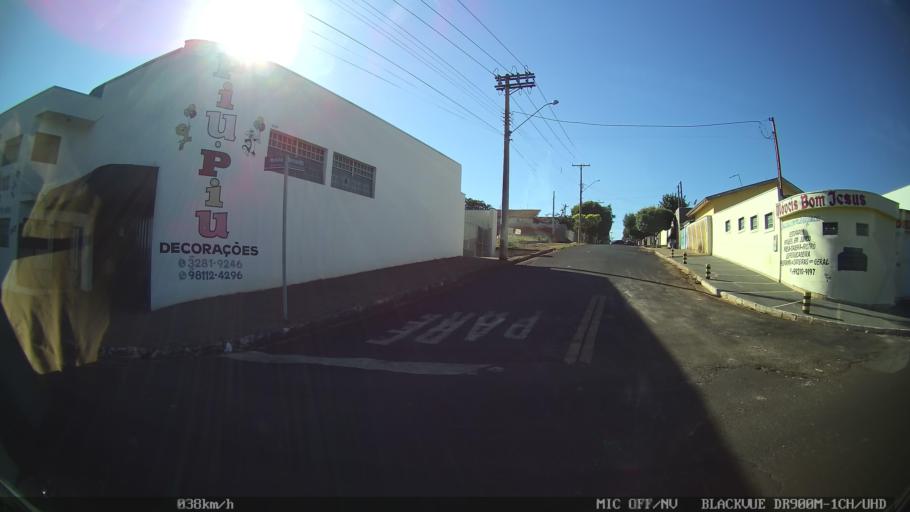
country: BR
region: Sao Paulo
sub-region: Olimpia
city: Olimpia
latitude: -20.7423
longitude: -48.8952
